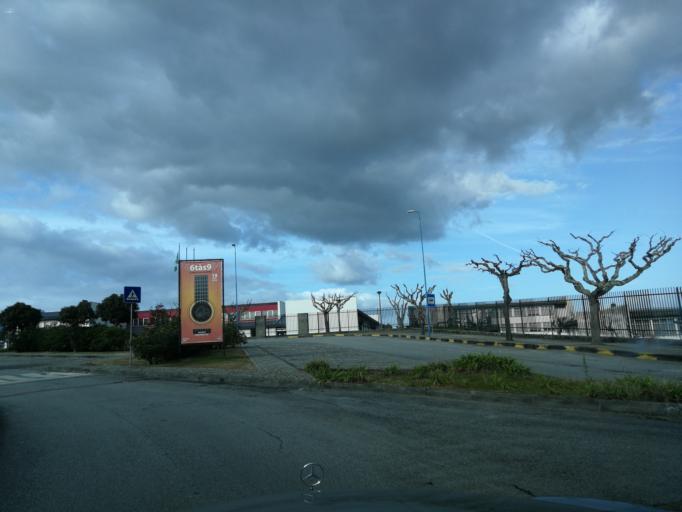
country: PT
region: Viana do Castelo
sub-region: Valenca
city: Valenza
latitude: 42.0283
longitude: -8.6384
